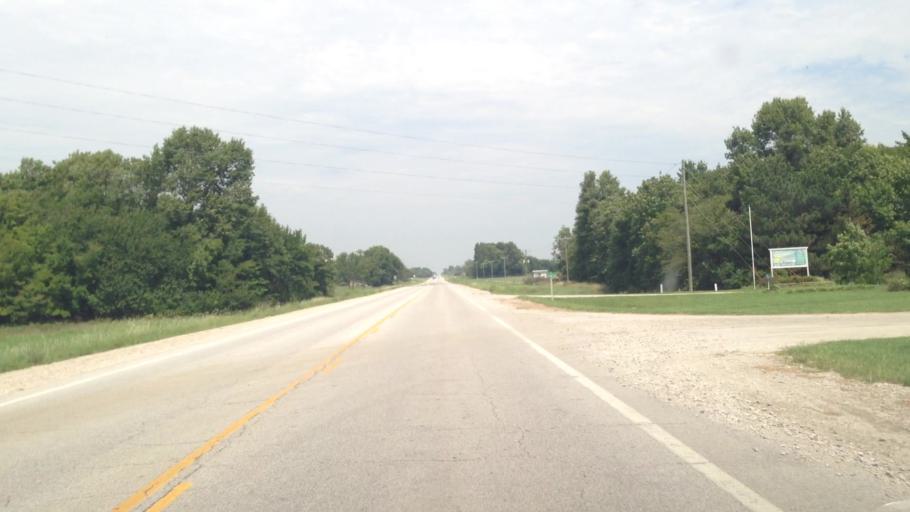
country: US
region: Kansas
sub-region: Neosho County
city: Erie
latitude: 37.5744
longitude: -95.2525
